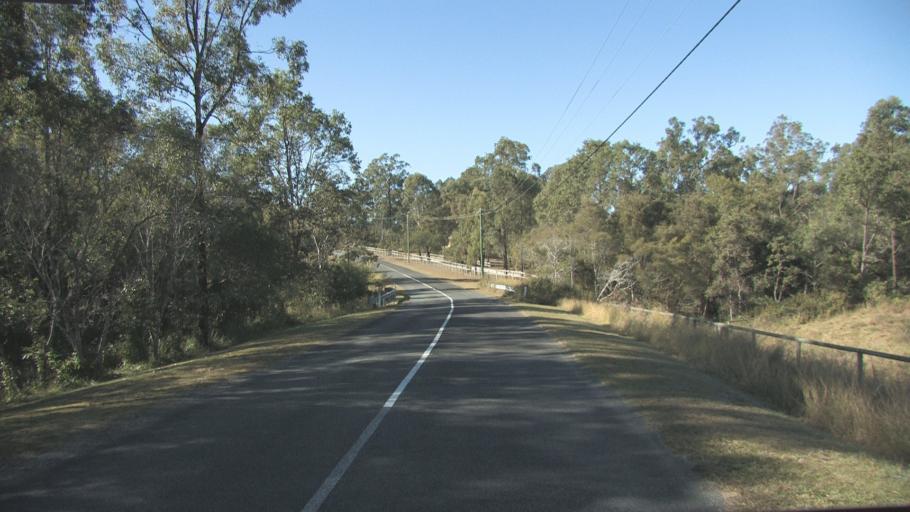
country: AU
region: Queensland
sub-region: Logan
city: North Maclean
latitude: -27.8115
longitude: 152.9677
